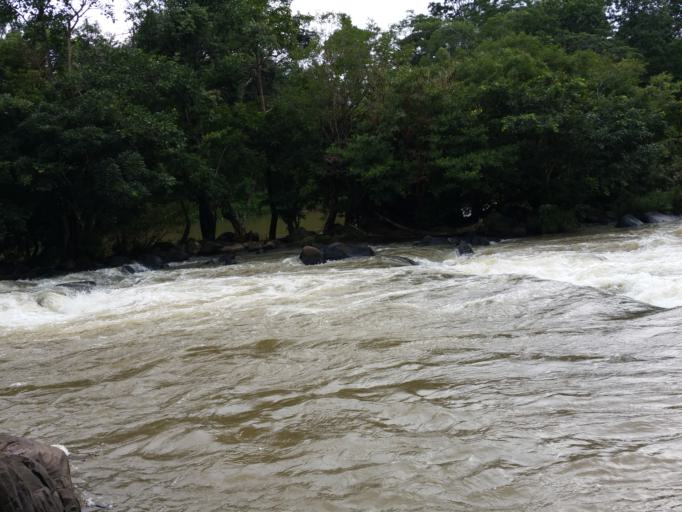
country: LA
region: Xekong
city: Thateng
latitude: 15.5309
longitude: 106.2726
